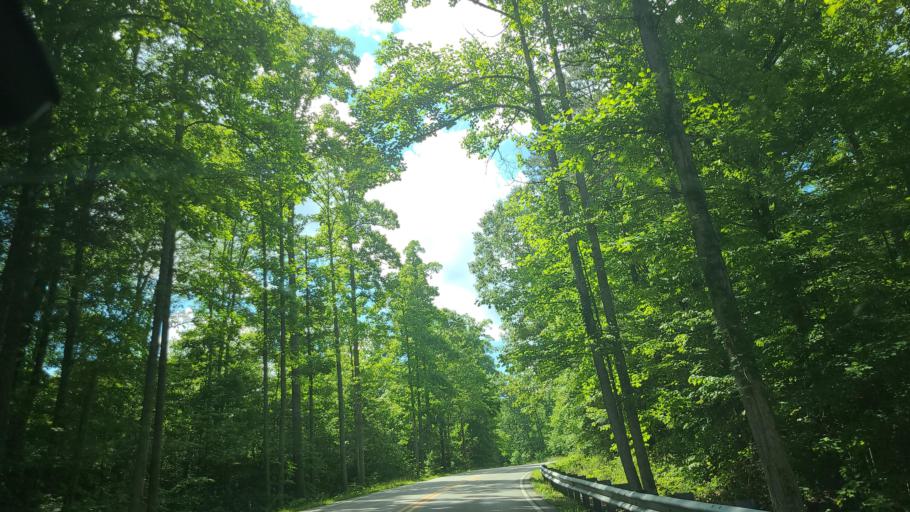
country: US
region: Kentucky
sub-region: Whitley County
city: Williamsburg
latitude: 36.8408
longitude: -84.2850
